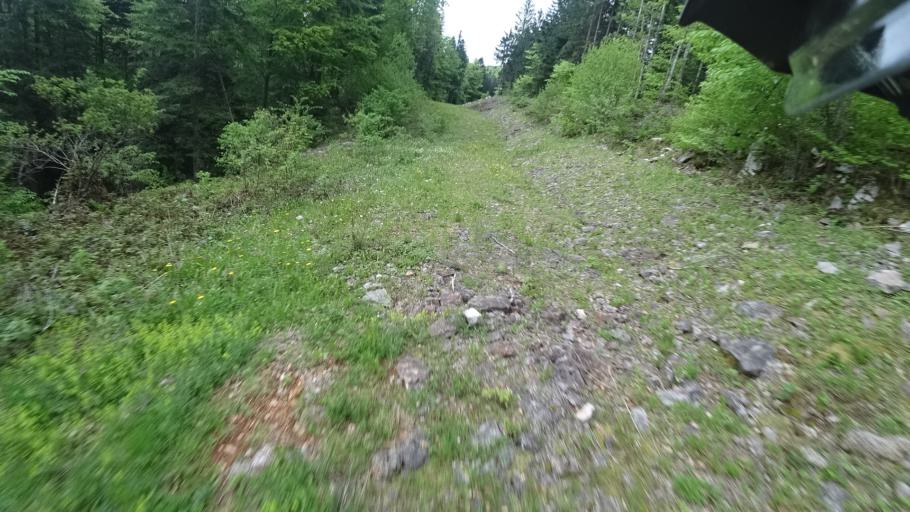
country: HR
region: Karlovacka
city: Plaski
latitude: 44.9591
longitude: 15.4121
